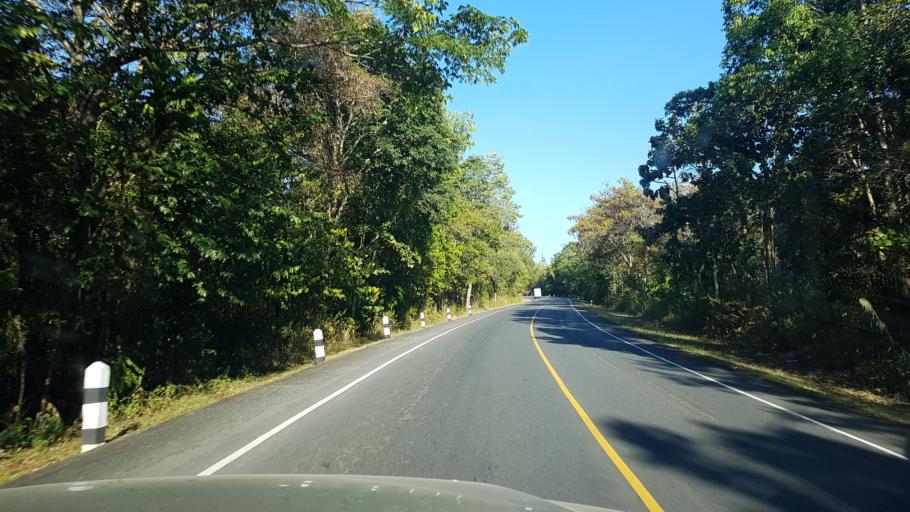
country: TH
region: Phetchabun
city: Nam Nao
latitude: 16.7520
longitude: 101.4561
